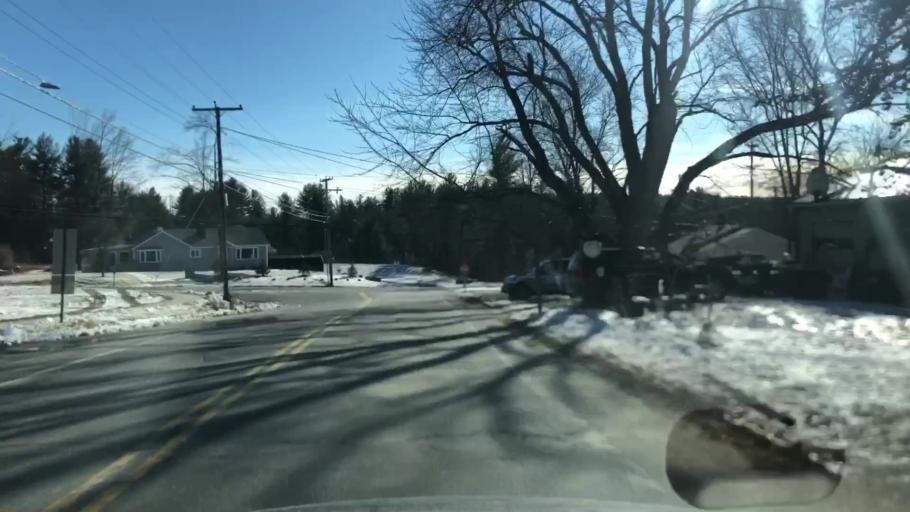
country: US
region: New Hampshire
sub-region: Hillsborough County
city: Milford
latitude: 42.8248
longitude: -71.6598
